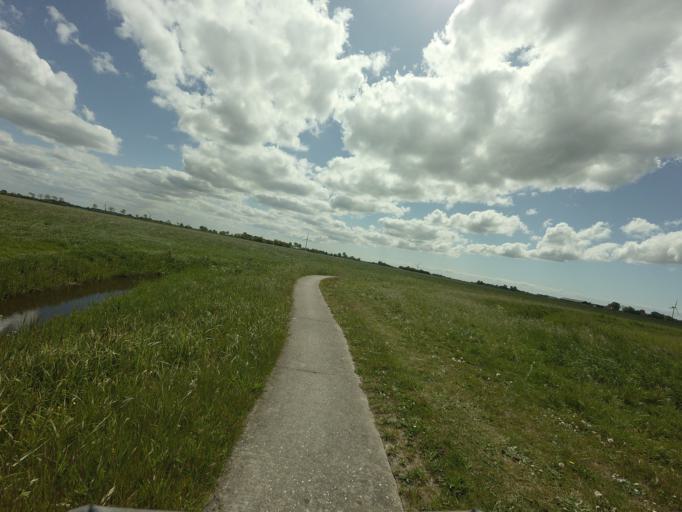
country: NL
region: Friesland
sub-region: Gemeente Littenseradiel
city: Wommels
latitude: 53.1302
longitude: 5.5715
